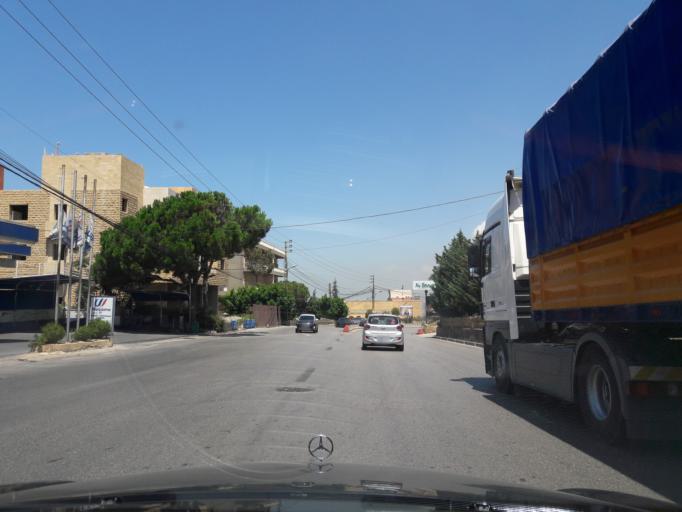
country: LB
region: Mont-Liban
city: Djounie
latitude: 33.9220
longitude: 35.6291
